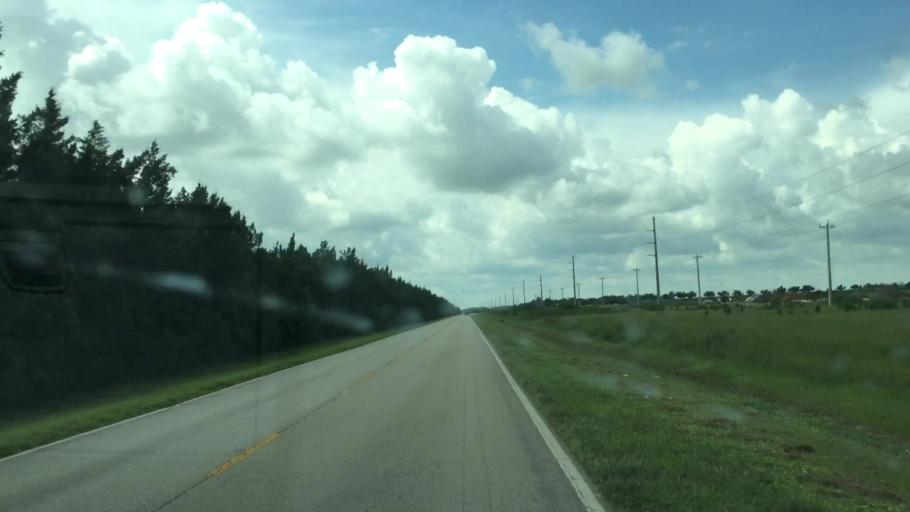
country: US
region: Florida
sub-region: Collier County
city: Immokalee
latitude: 26.3466
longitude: -81.4168
